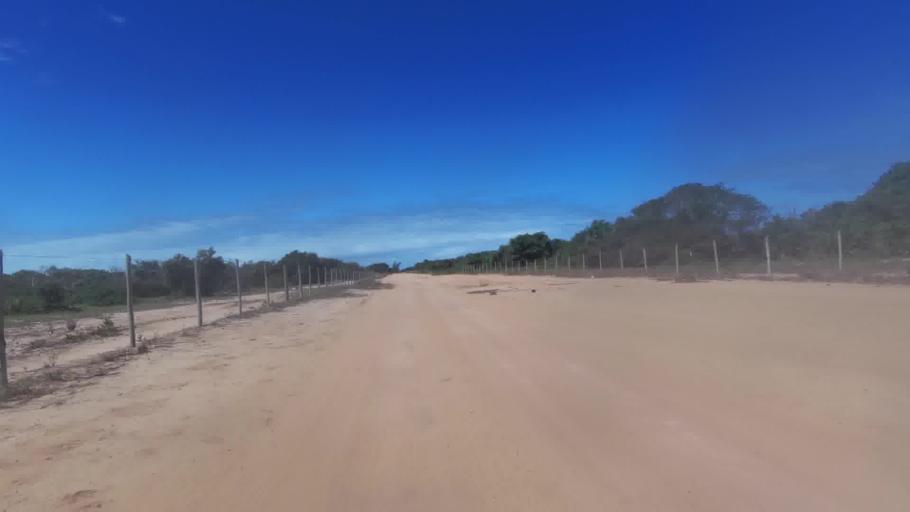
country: BR
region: Espirito Santo
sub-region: Marataizes
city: Marataizes
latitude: -21.1978
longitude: -40.9440
